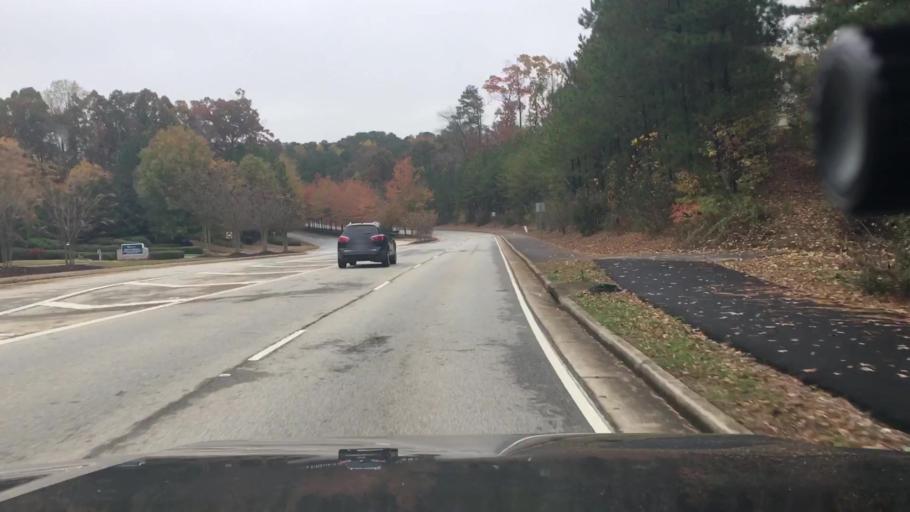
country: US
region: Georgia
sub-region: Coweta County
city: East Newnan
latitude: 33.3901
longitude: -84.7445
